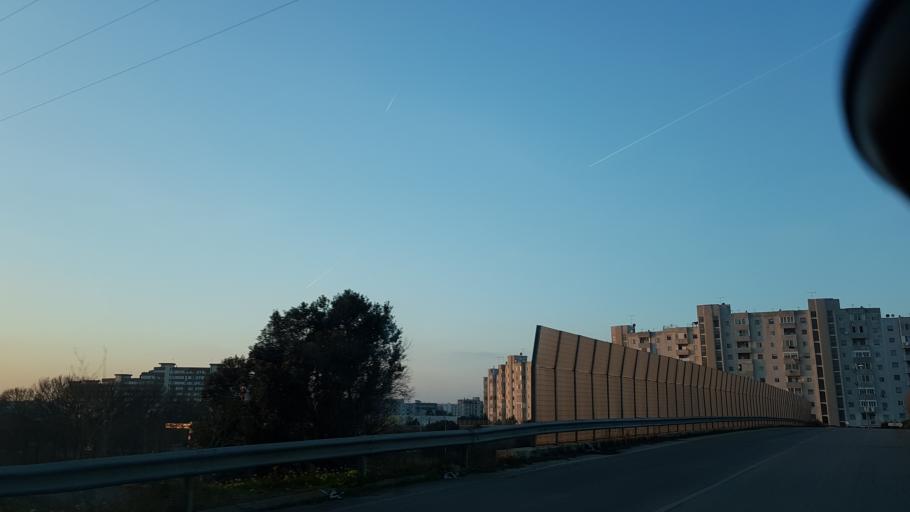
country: IT
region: Apulia
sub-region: Provincia di Brindisi
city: La Rosa
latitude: 40.6179
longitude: 17.9450
